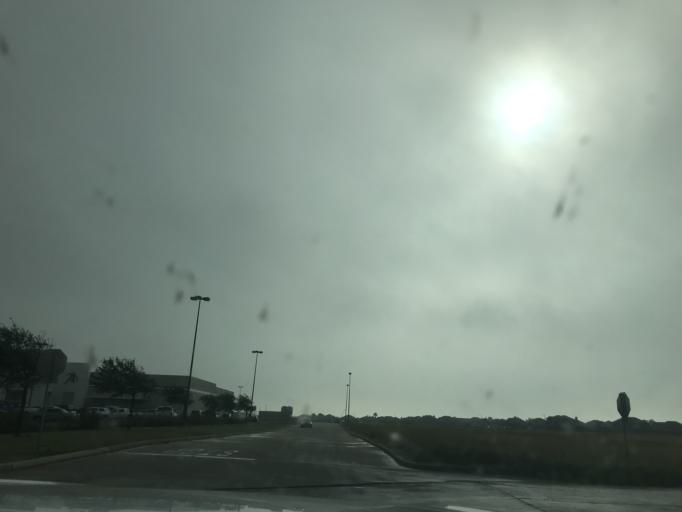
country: US
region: Texas
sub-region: San Patricio County
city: Portland
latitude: 27.8932
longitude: -97.3085
